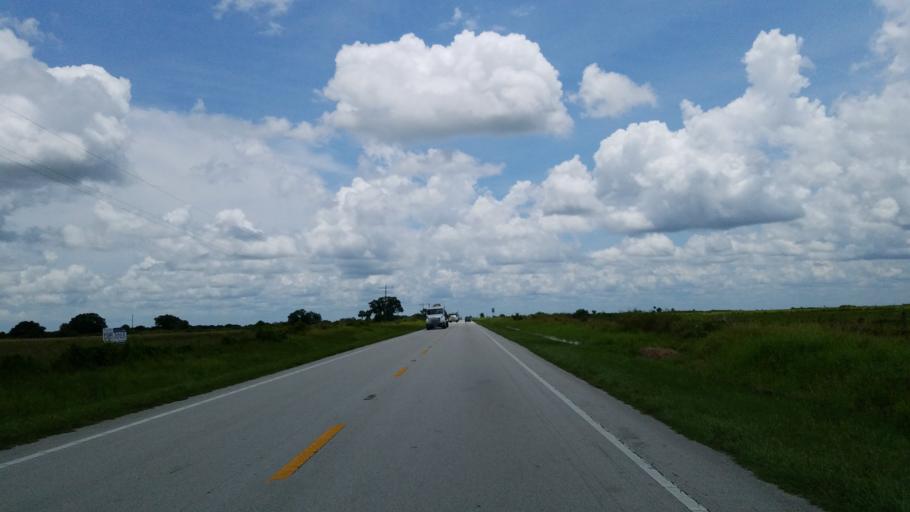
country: US
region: Florida
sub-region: Polk County
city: Babson Park
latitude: 27.7732
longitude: -81.1158
